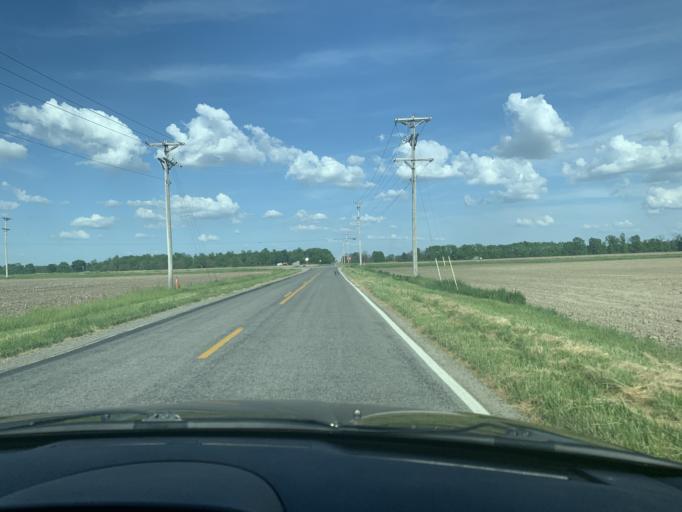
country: US
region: Ohio
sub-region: Logan County
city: De Graff
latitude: 40.2421
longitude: -83.9788
